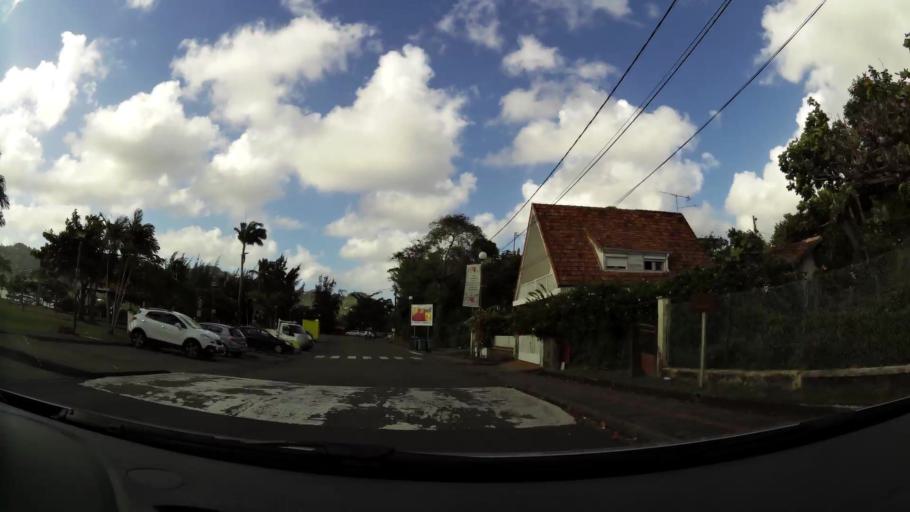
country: MQ
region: Martinique
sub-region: Martinique
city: Le Robert
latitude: 14.6758
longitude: -60.9388
